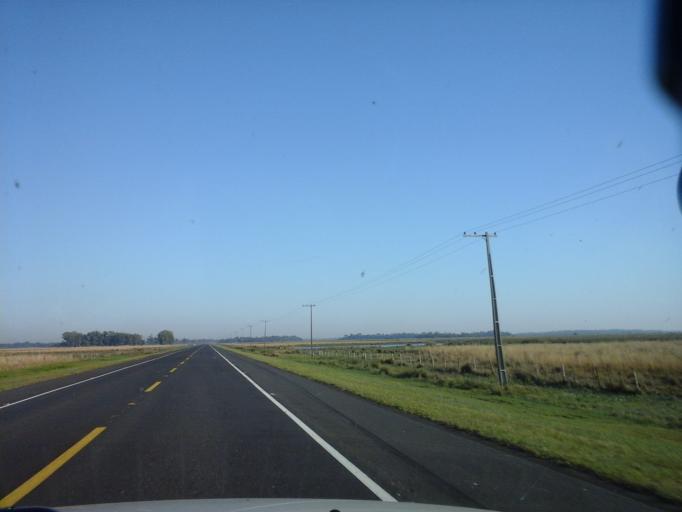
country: PY
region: Neembucu
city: Pilar
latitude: -26.8665
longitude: -57.9359
